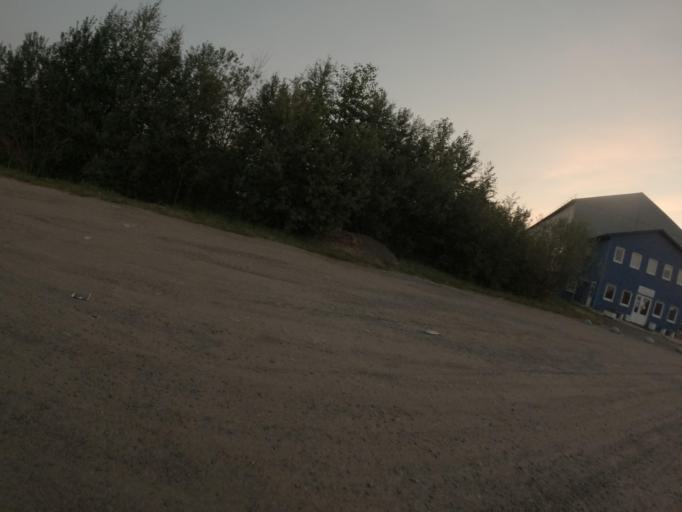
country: RU
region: Leningrad
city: Yanino Vtoroye
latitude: 59.9360
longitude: 30.5926
